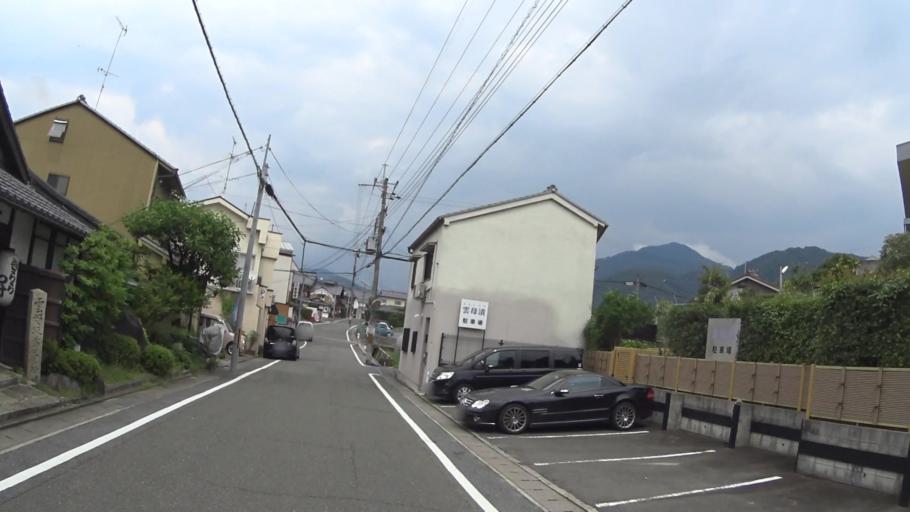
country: JP
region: Kyoto
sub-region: Kyoto-shi
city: Kamigyo-ku
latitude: 35.0444
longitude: 135.7936
